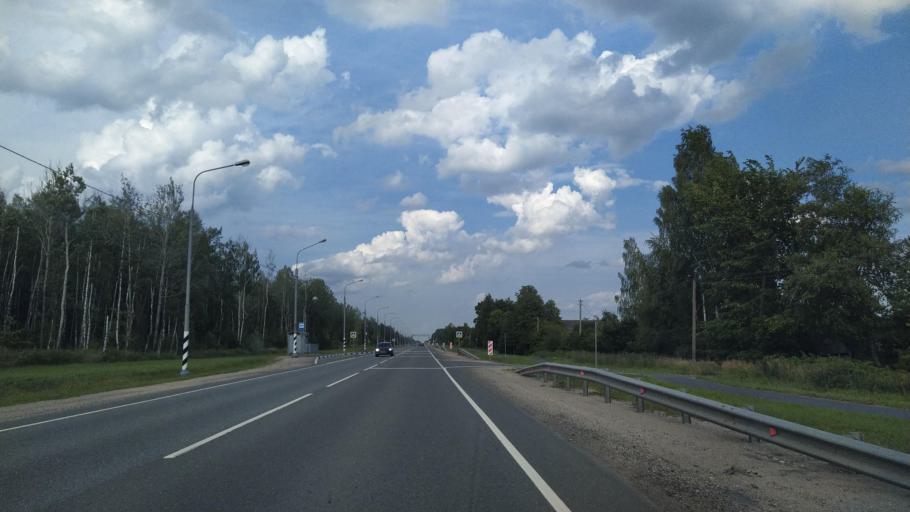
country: RU
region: Novgorod
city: Shimsk
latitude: 58.2566
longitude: 30.8008
